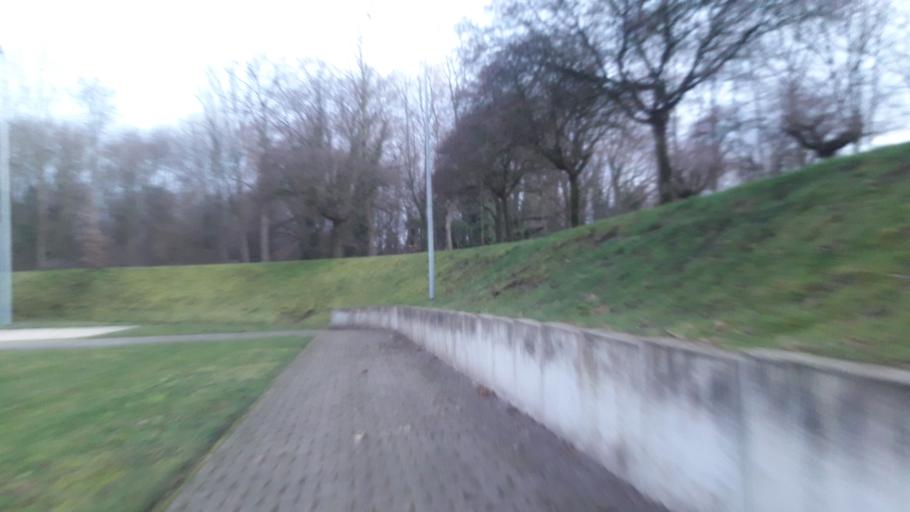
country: DE
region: North Rhine-Westphalia
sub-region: Regierungsbezirk Detmold
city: Paderborn
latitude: 51.7284
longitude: 8.7411
